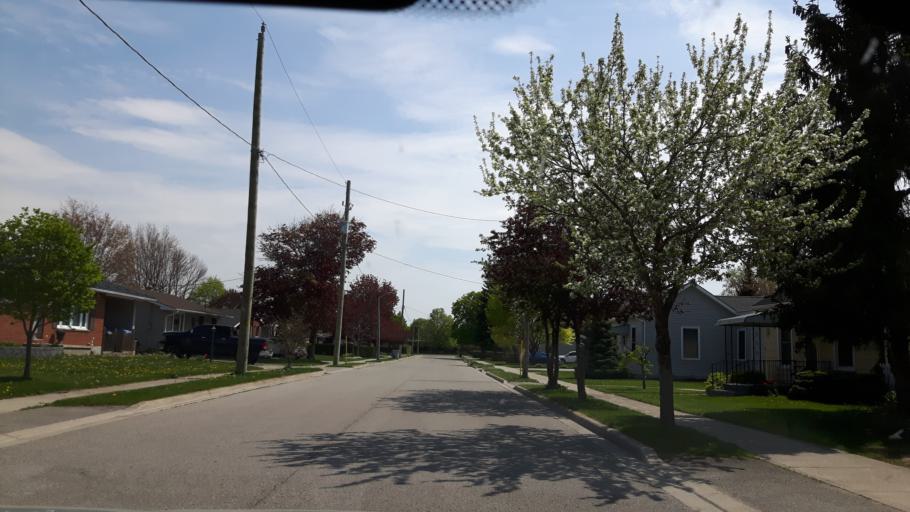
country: CA
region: Ontario
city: Goderich
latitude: 43.7373
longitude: -81.7179
